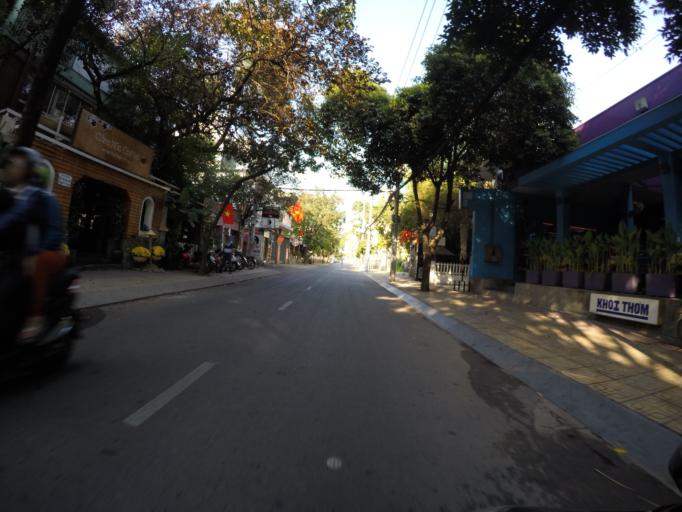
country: VN
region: Ho Chi Minh City
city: Quan Ba
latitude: 10.7806
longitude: 106.6901
